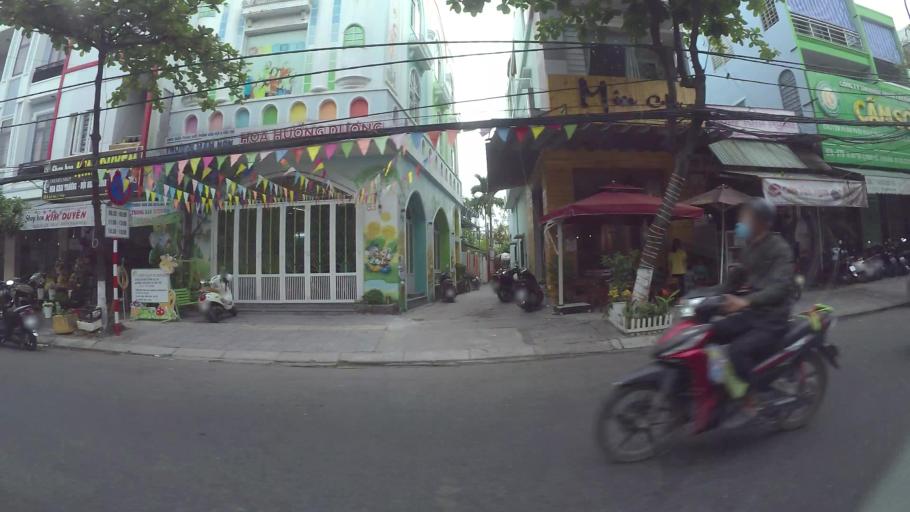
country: VN
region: Da Nang
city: Thanh Khe
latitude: 16.0673
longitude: 108.1920
